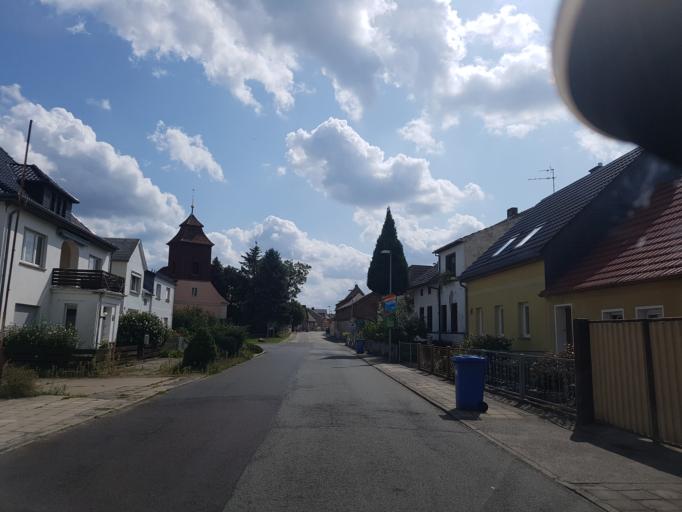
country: DE
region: Brandenburg
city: Gross Kreutz
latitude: 52.3382
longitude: 12.7239
